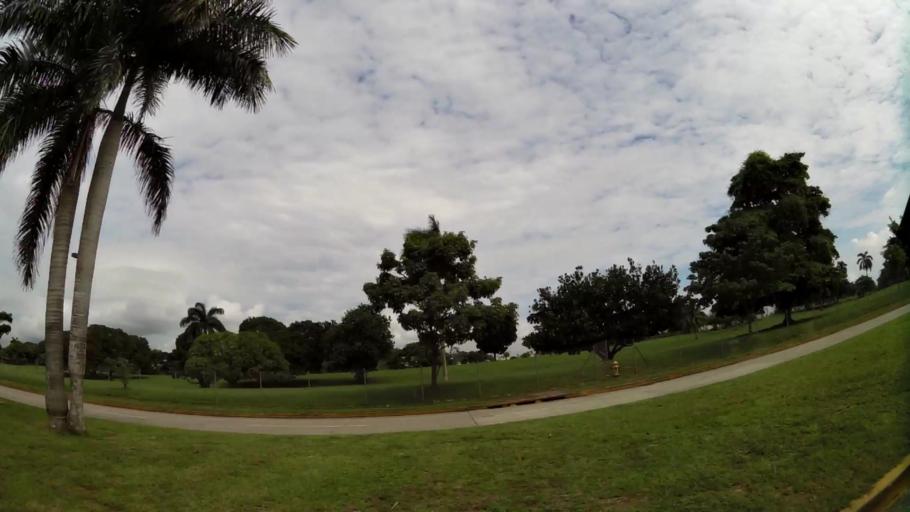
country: PA
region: Panama
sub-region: Distrito de Panama
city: Ancon
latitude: 8.9406
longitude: -79.5471
